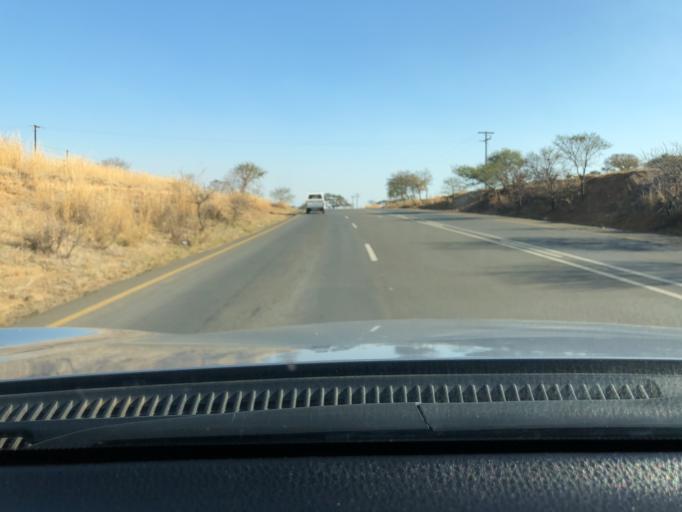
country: ZA
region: KwaZulu-Natal
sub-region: uMzinyathi District Municipality
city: Glencoe
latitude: -28.3050
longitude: 30.0612
